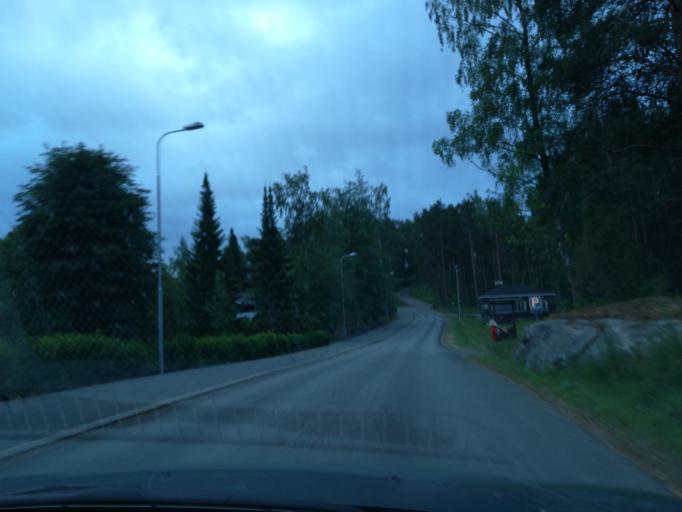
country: FI
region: Southern Savonia
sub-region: Mikkeli
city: Ristiina
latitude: 61.4989
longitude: 27.2695
